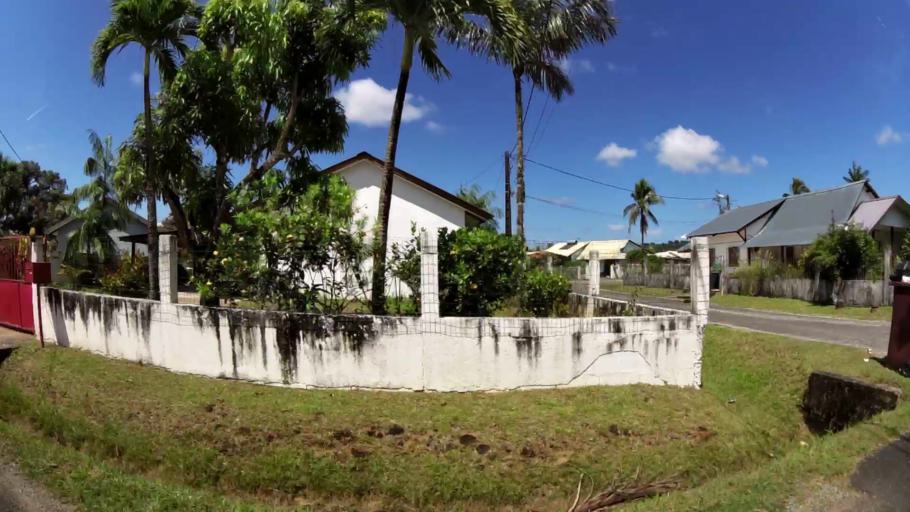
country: GF
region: Guyane
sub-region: Guyane
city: Matoury
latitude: 4.8490
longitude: -52.3275
